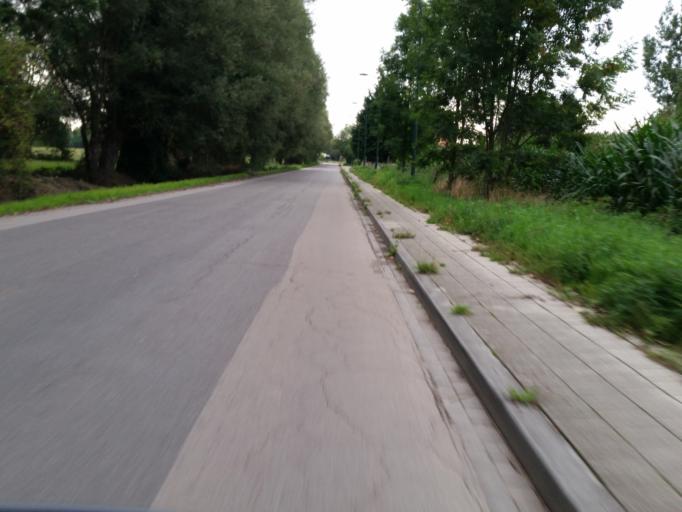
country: BE
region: Flanders
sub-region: Provincie Vlaams-Brabant
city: Zemst
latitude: 50.9525
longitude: 4.4602
